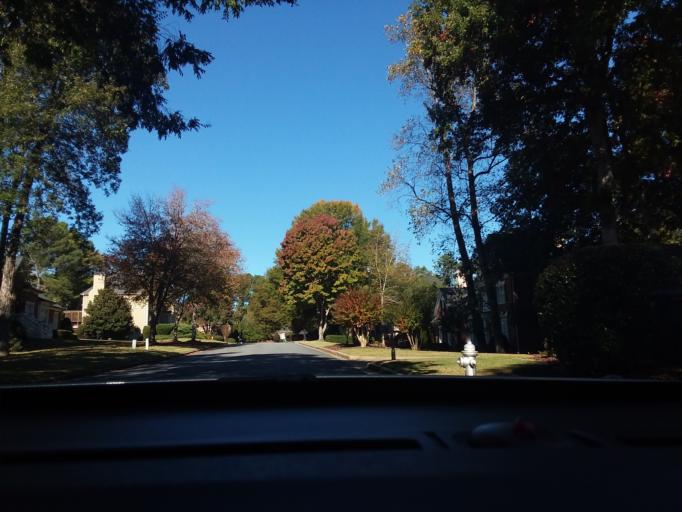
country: US
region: Georgia
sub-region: Fulton County
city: Johns Creek
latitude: 34.0249
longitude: -84.1860
